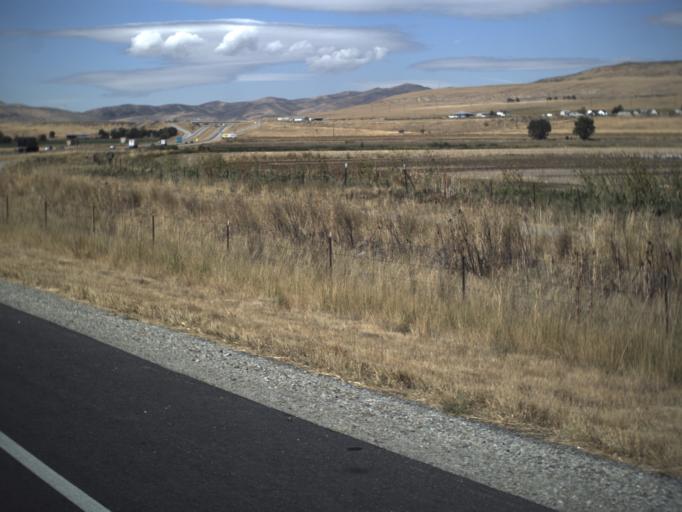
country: US
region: Utah
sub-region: Box Elder County
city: Tremonton
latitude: 41.7115
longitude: -112.2051
